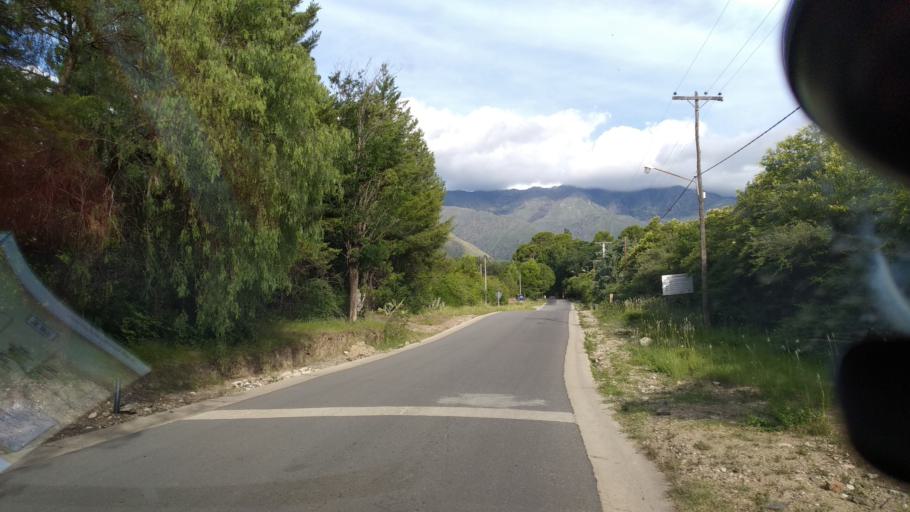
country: AR
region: Cordoba
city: Villa Las Rosas
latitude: -32.0262
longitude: -65.0151
